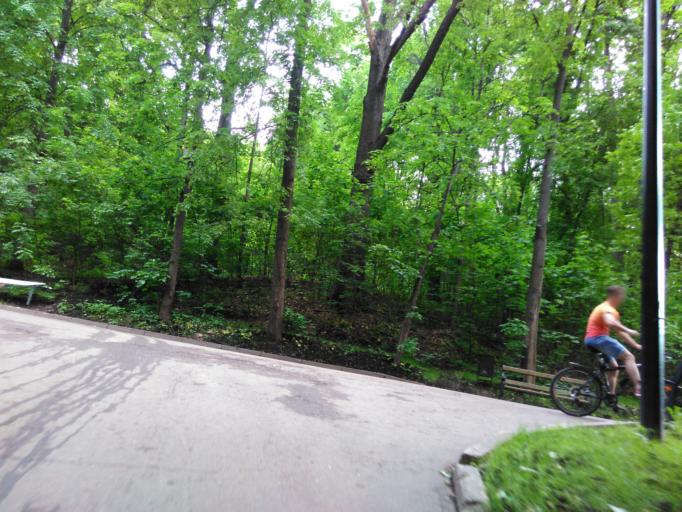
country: RU
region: Moscow
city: Luzhniki
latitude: 55.7085
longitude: 37.5593
